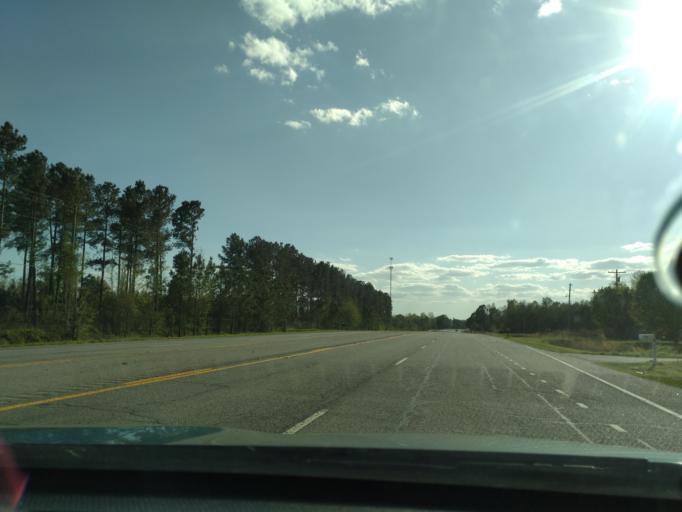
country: US
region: South Carolina
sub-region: Williamsburg County
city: Kingstree
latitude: 33.6444
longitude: -79.8944
